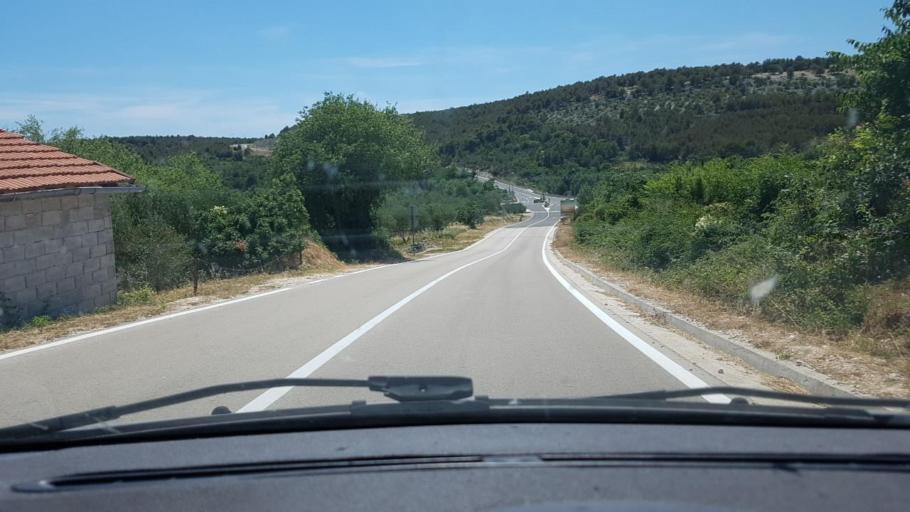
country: HR
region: Sibensko-Kniniska
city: Zaton
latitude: 43.8445
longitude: 15.9017
